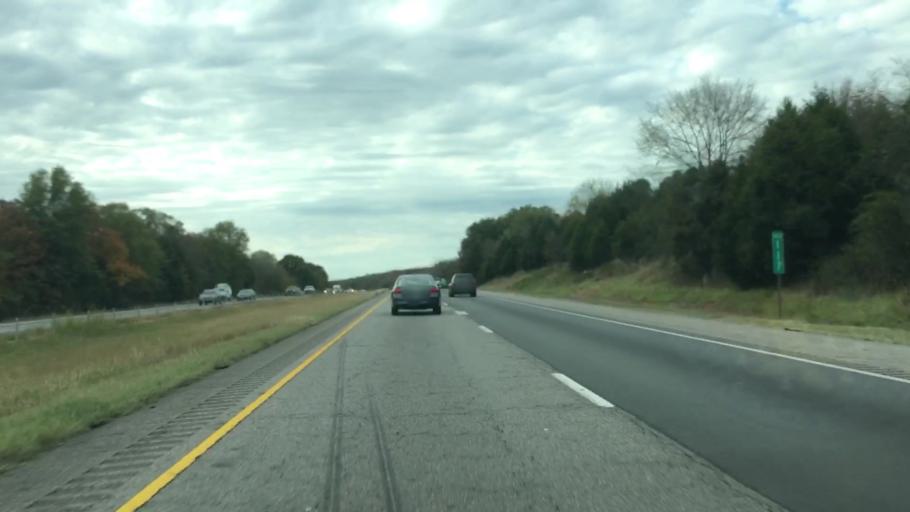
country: US
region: Arkansas
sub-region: Faulkner County
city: Conway
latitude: 35.1558
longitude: -92.5620
